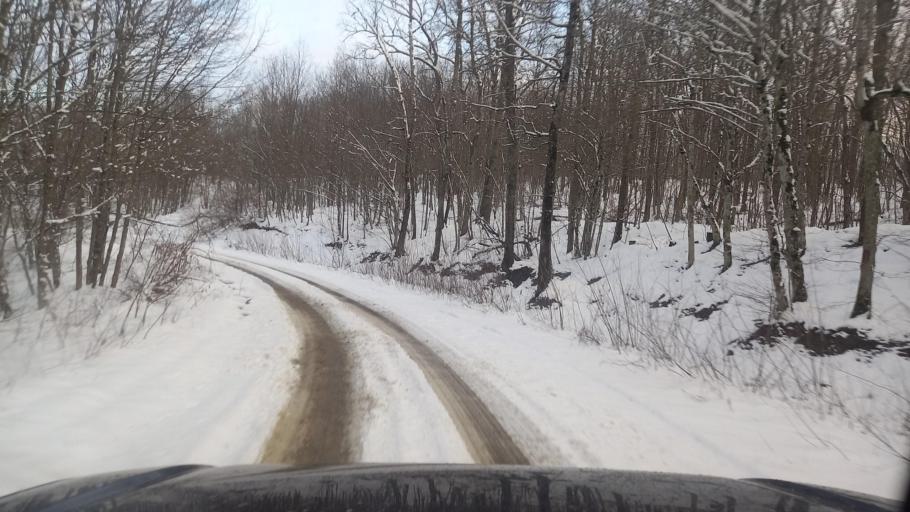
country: RU
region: Krasnodarskiy
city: Smolenskaya
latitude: 44.6784
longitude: 38.7684
